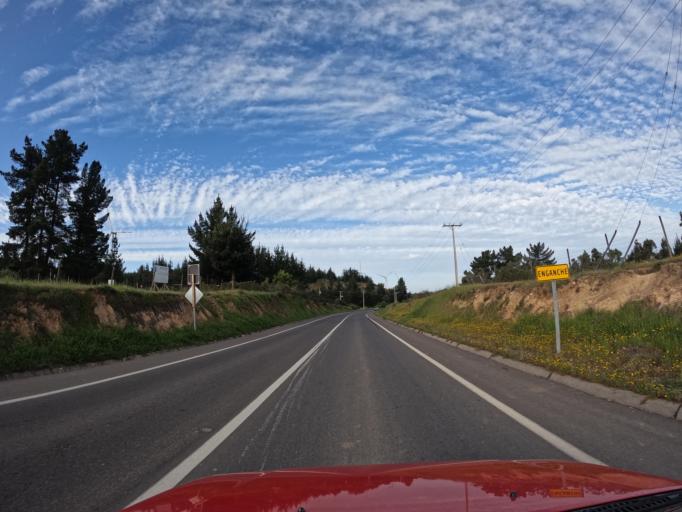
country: CL
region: Valparaiso
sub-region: San Antonio Province
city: San Antonio
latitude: -34.0508
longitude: -71.6221
